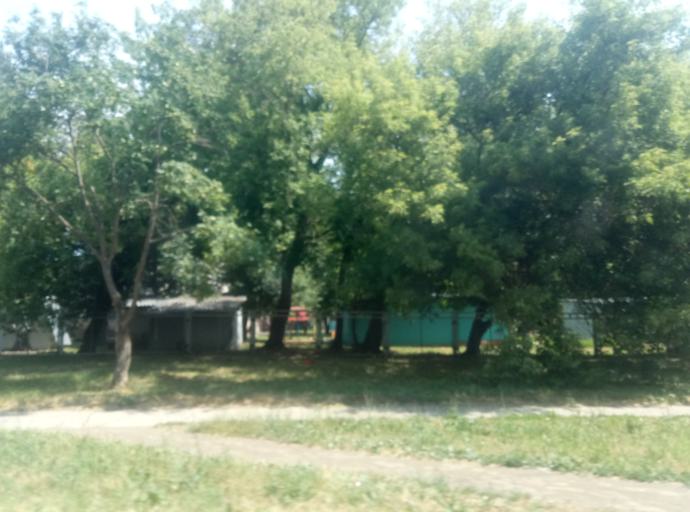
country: RU
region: Tula
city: Kireyevsk
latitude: 53.9253
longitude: 37.9355
